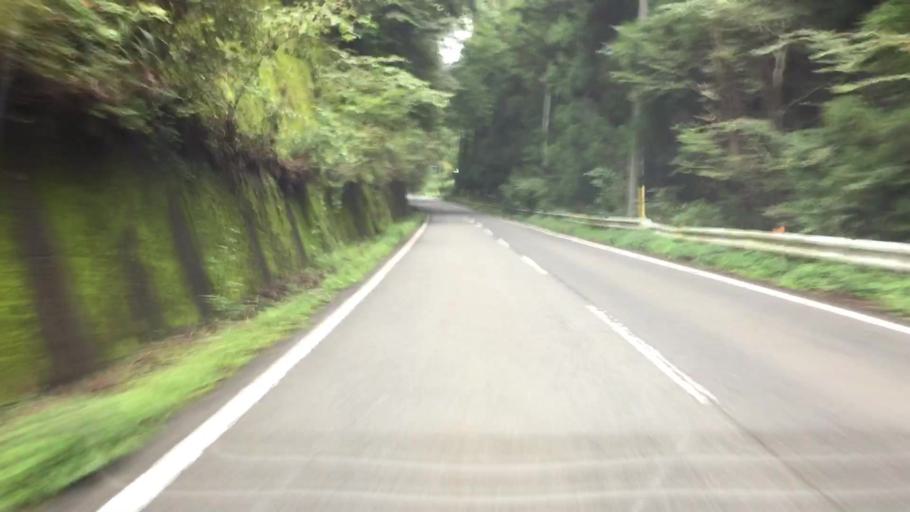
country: JP
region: Tochigi
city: Imaichi
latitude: 36.7608
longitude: 139.6818
